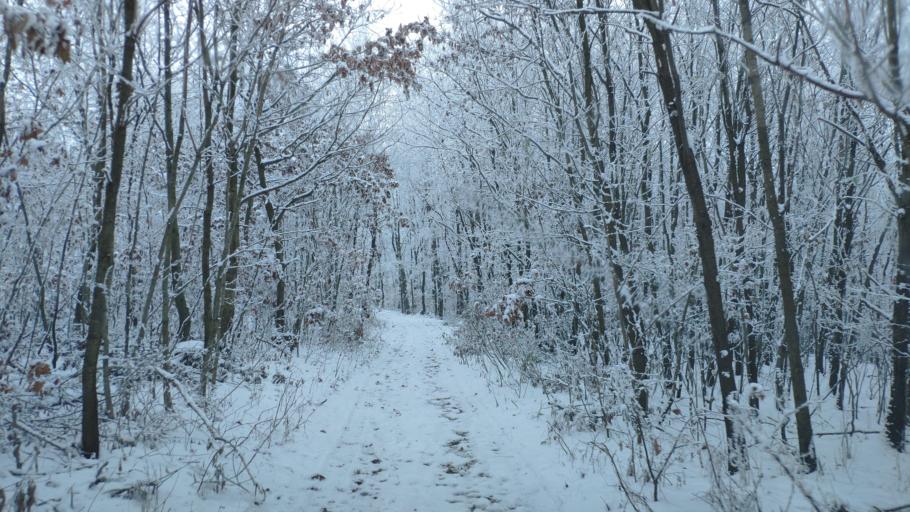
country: SK
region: Kosicky
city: Kosice
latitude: 48.6562
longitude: 21.1842
